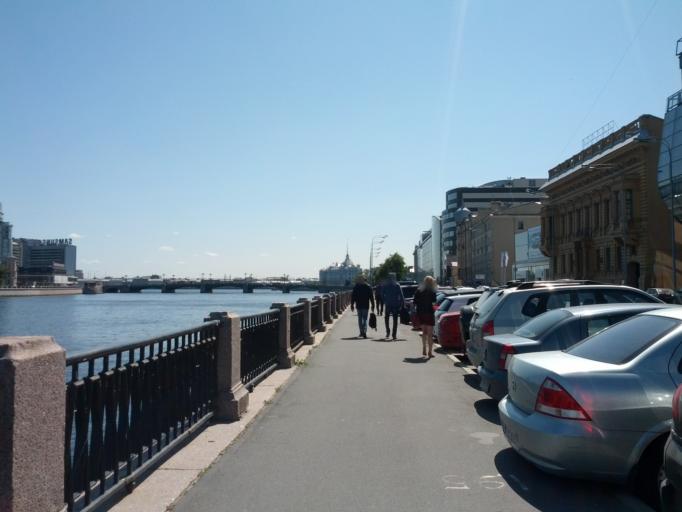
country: RU
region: St.-Petersburg
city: Petrogradka
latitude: 59.9627
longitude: 30.3348
